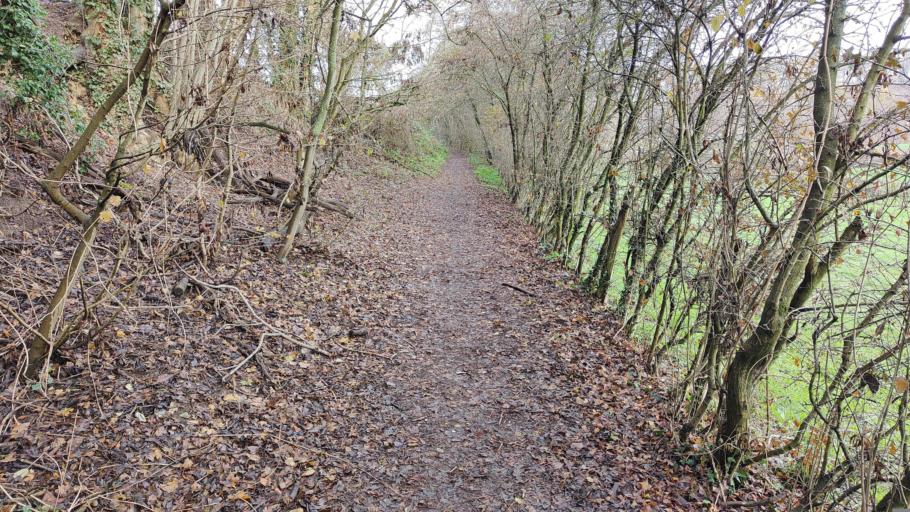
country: NL
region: Limburg
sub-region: Valkenburg aan de Geul
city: Berg
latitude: 50.8339
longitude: 5.7686
